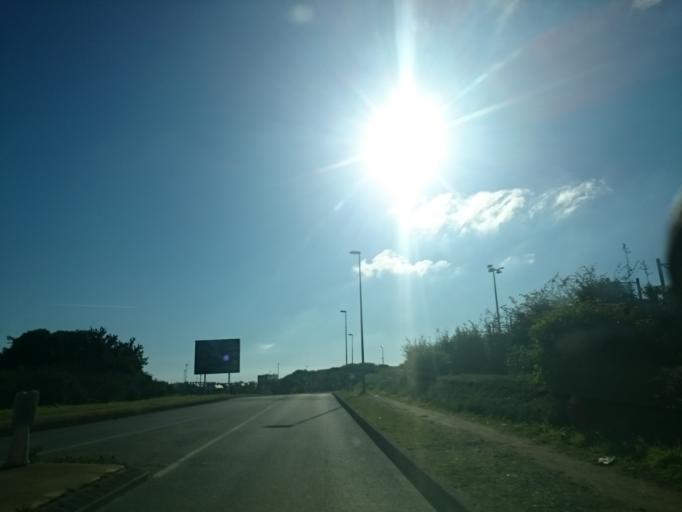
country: FR
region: Brittany
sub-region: Departement du Finistere
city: Brest
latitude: 48.4236
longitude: -4.4747
